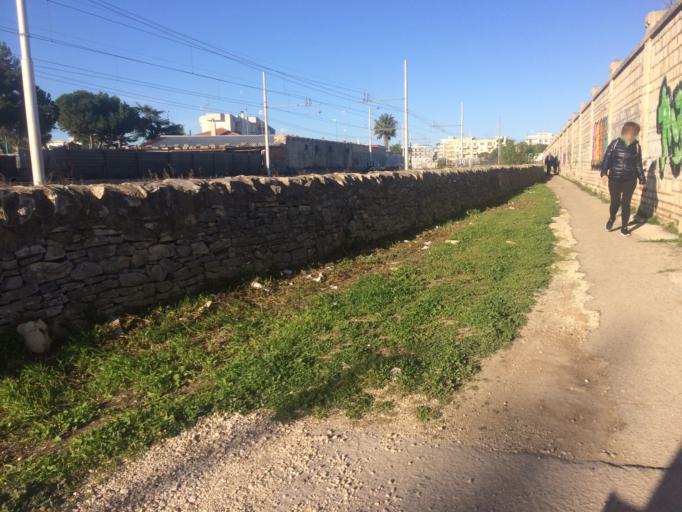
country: IT
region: Apulia
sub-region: Provincia di Bari
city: Terlizzi
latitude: 41.1276
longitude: 16.5543
